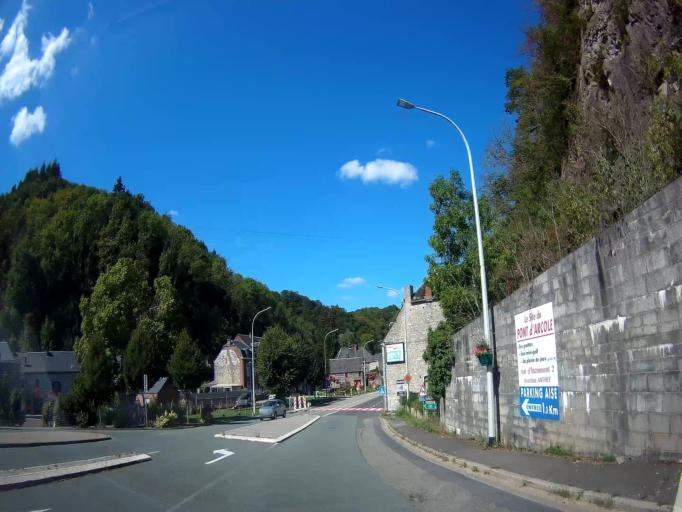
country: BE
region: Wallonia
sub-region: Province de Namur
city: Hastiere-Lavaux
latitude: 50.2172
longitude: 4.8250
